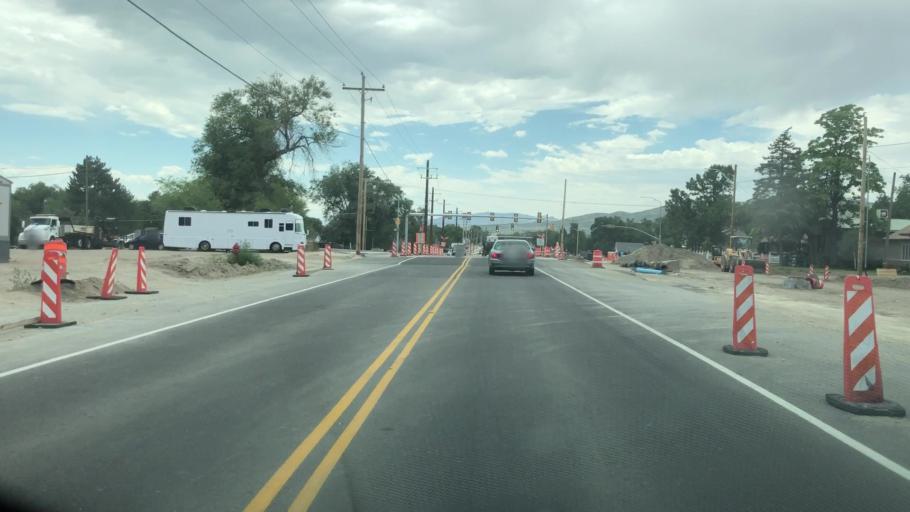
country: US
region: Utah
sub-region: Salt Lake County
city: Riverton
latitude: 40.5090
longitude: -111.9385
